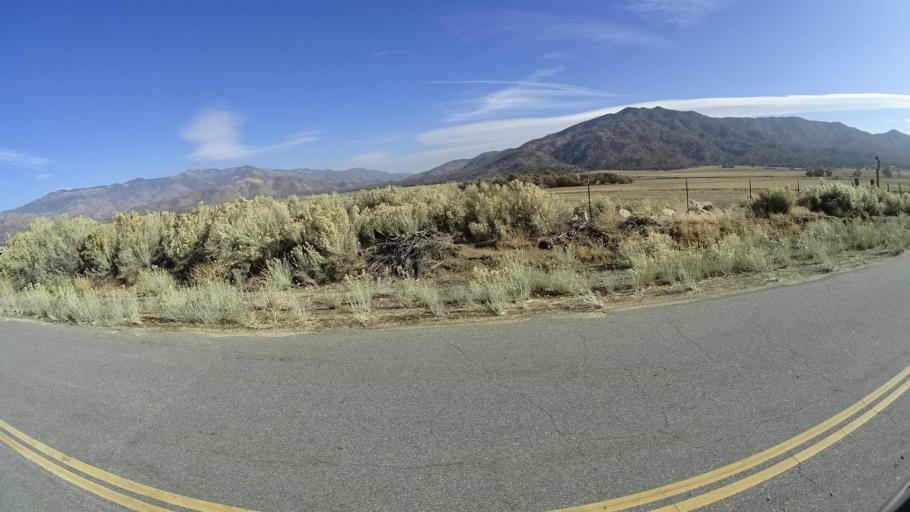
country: US
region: California
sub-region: Kern County
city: Bodfish
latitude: 35.4033
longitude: -118.5456
